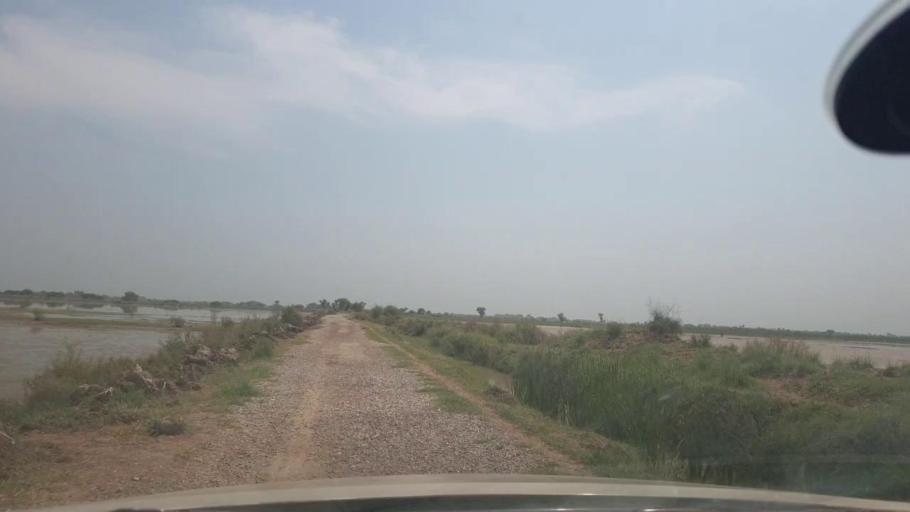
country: PK
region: Sindh
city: Jacobabad
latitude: 28.2296
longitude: 68.3930
